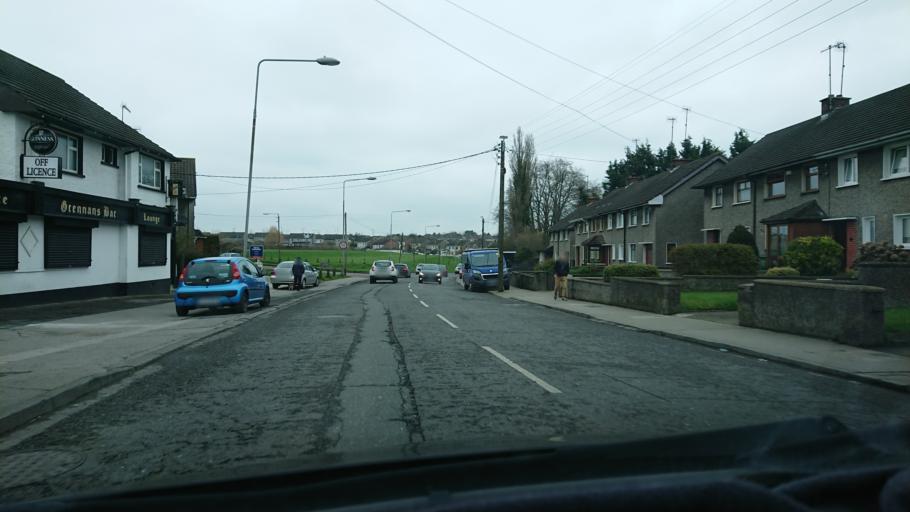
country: IE
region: Leinster
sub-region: Lu
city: Drogheda
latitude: 53.7207
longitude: -6.3408
